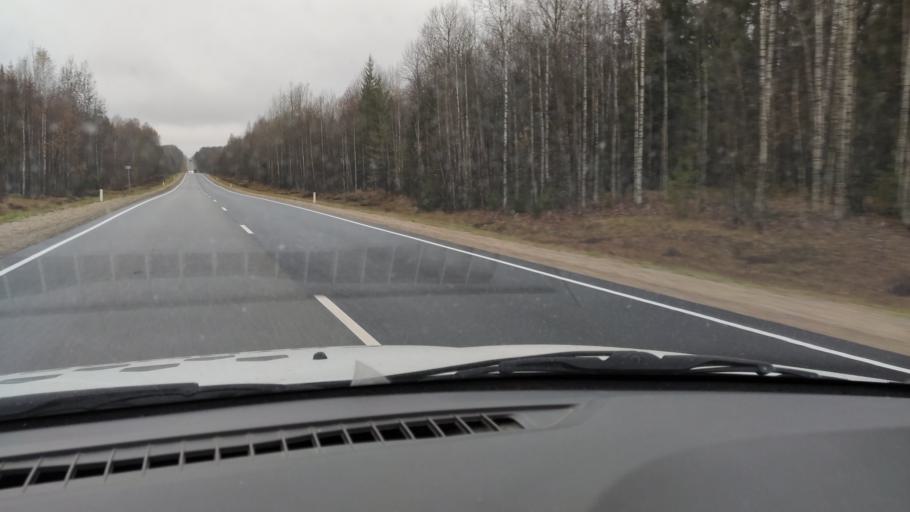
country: RU
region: Kirov
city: Chernaya Kholunitsa
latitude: 58.7876
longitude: 51.8964
